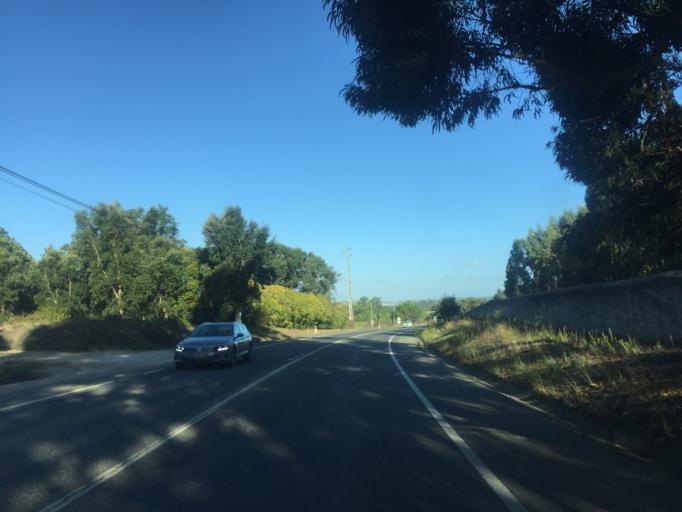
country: PT
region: Lisbon
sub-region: Azambuja
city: Alcoentre
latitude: 39.1751
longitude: -8.9361
